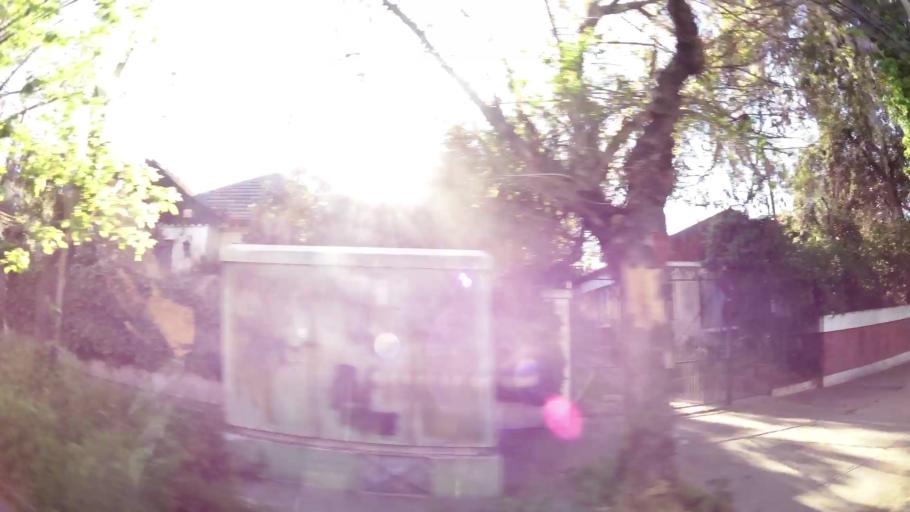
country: CL
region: Santiago Metropolitan
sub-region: Provincia de Santiago
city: Villa Presidente Frei, Nunoa, Santiago, Chile
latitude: -33.4491
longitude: -70.5676
